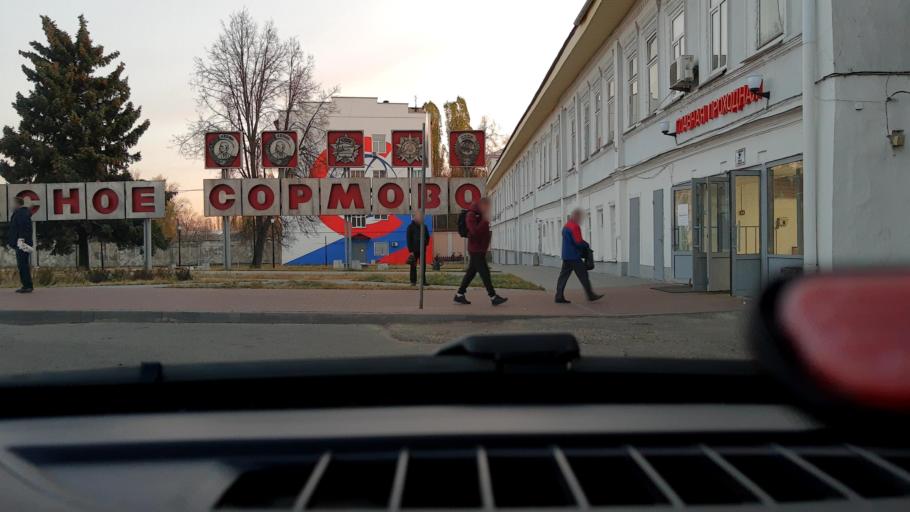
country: RU
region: Nizjnij Novgorod
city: Neklyudovo
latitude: 56.3591
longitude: 43.8706
